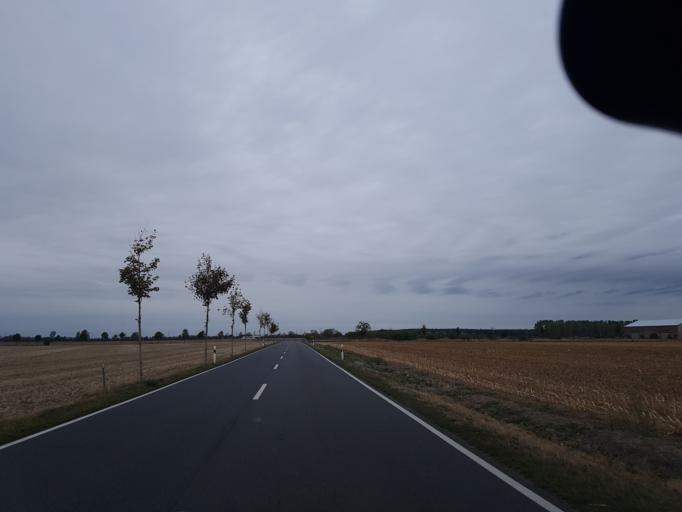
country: DE
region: Saxony-Anhalt
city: Prettin
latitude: 51.6697
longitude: 12.9159
